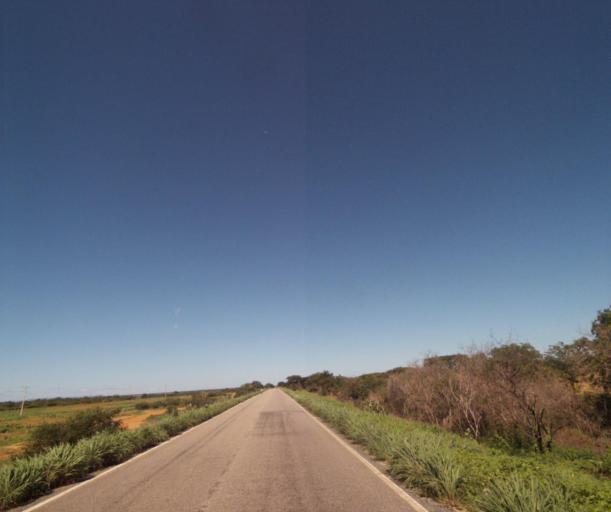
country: BR
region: Bahia
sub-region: Palmas De Monte Alto
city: Palmas de Monte Alto
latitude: -14.2582
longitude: -43.2679
